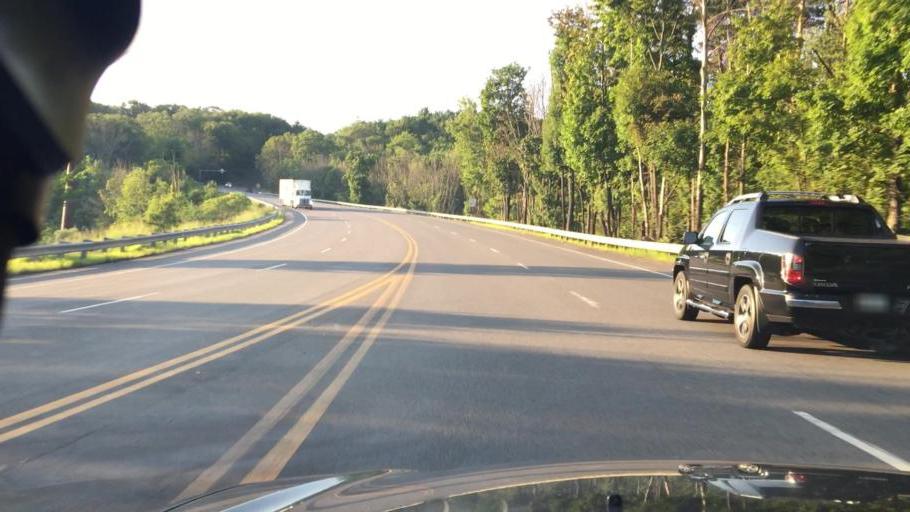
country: US
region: Pennsylvania
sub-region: Luzerne County
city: Harleigh
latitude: 41.0228
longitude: -75.9641
